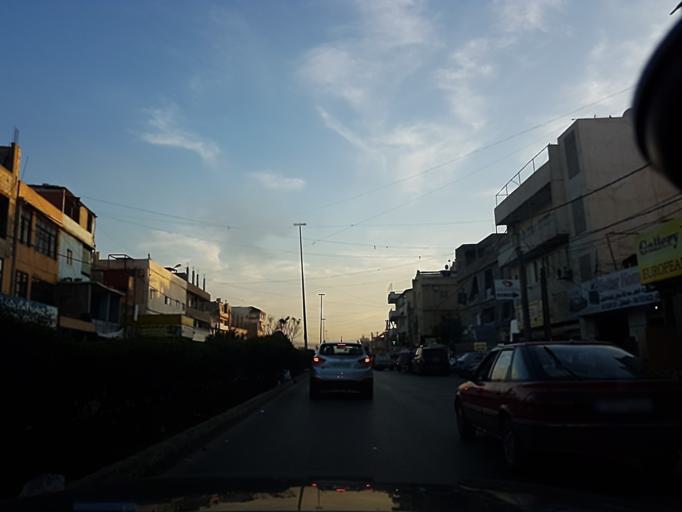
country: LB
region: Beyrouth
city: Beirut
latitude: 33.8474
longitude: 35.4851
